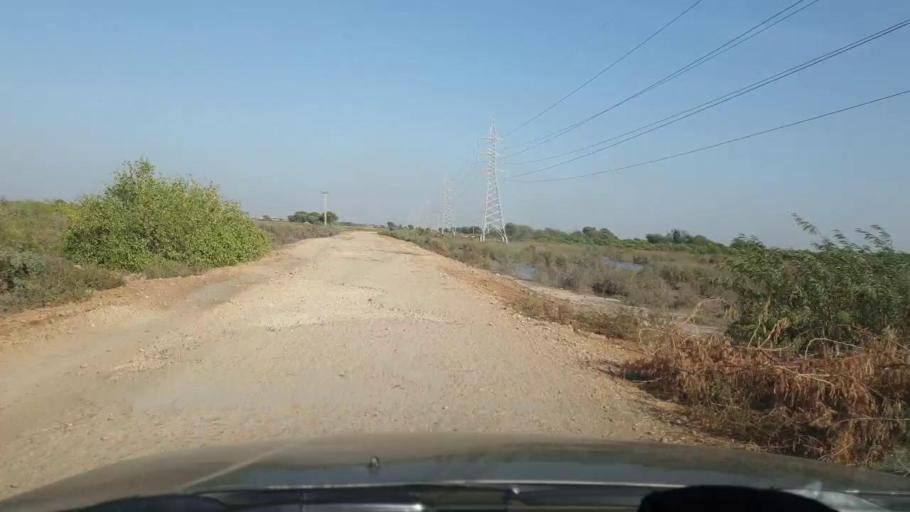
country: PK
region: Sindh
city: Bulri
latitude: 25.1088
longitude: 68.2479
